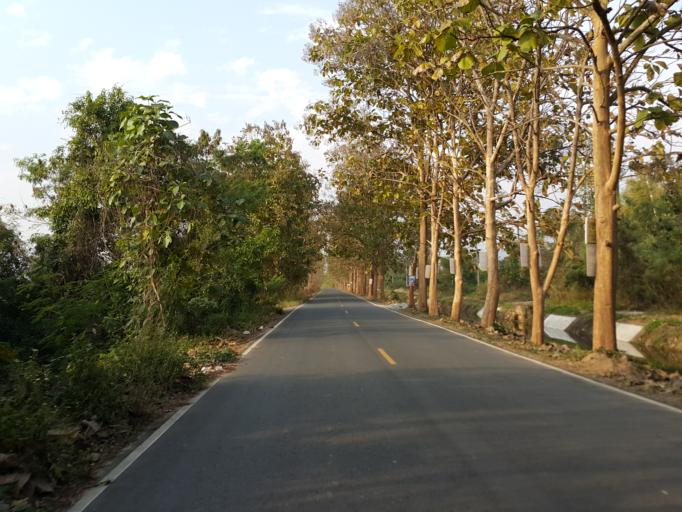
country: TH
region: Chiang Mai
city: San Sai
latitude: 18.8834
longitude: 99.1414
